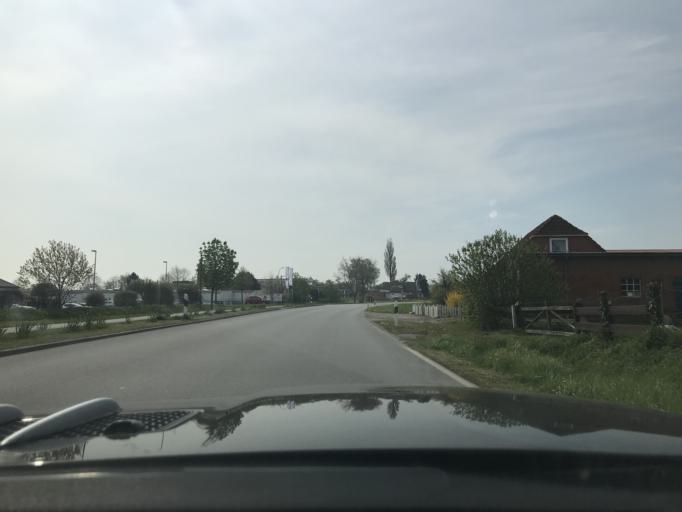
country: DE
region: Schleswig-Holstein
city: Grube
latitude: 54.2246
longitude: 11.0345
